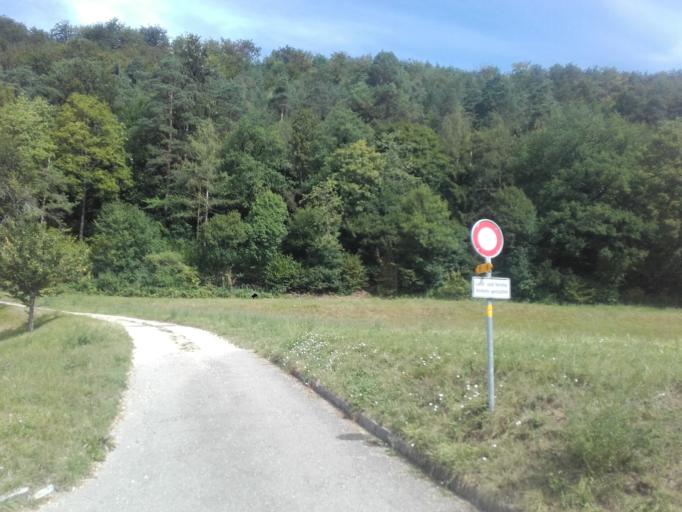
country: CH
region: Solothurn
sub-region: Bezirk Thal
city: Balsthal
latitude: 47.3195
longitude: 7.6890
